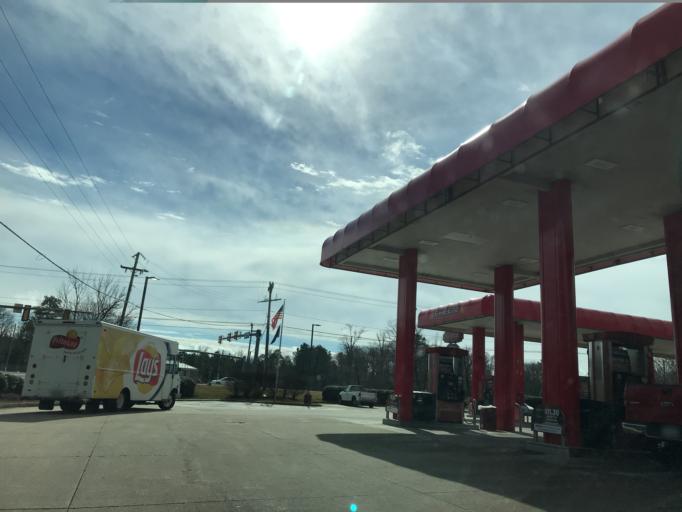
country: US
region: Virginia
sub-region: King George County
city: Dahlgren
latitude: 38.3534
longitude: -77.0486
